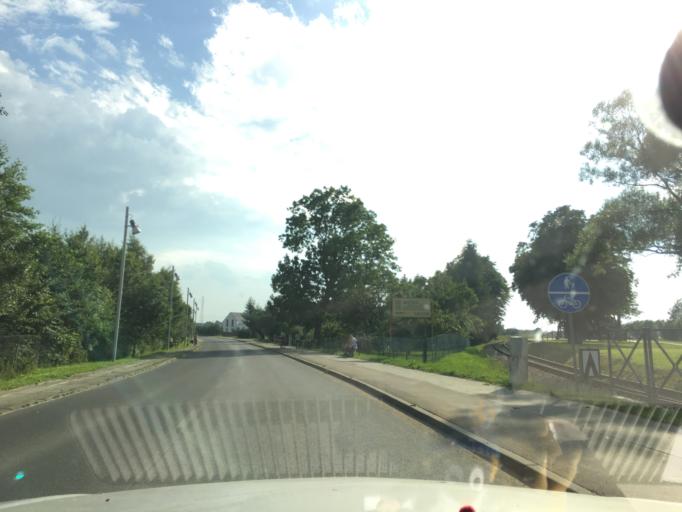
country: PL
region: West Pomeranian Voivodeship
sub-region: Powiat gryficki
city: Rewal
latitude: 54.0909
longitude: 15.0706
